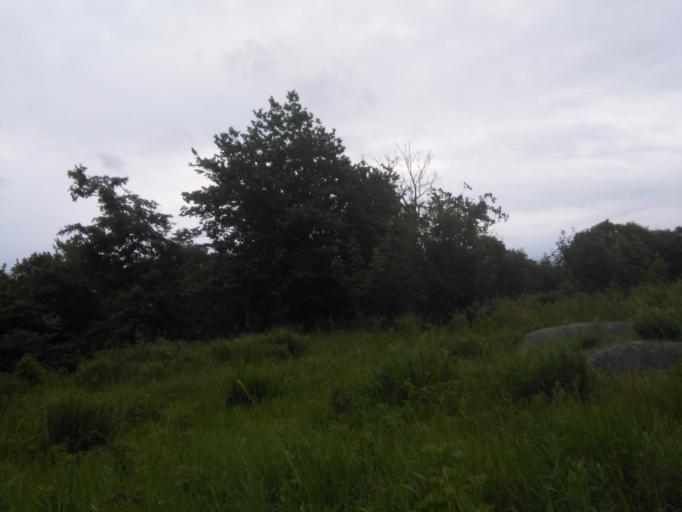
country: DK
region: Capital Region
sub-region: Bornholm Kommune
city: Akirkeby
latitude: 55.1141
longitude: 14.9068
